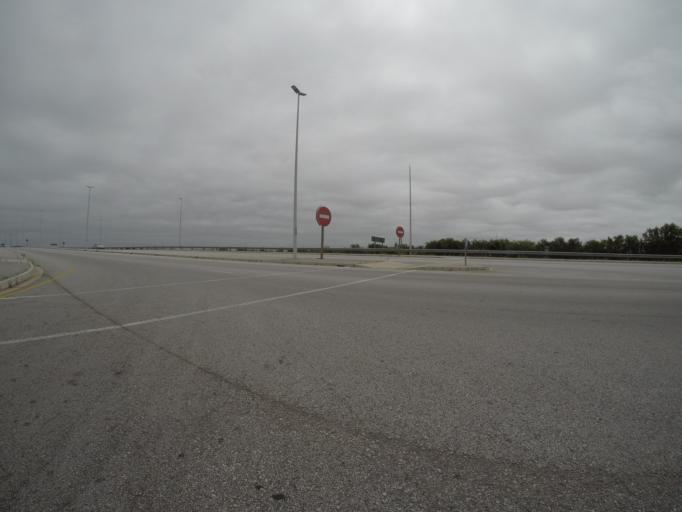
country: ZA
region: Eastern Cape
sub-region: Nelson Mandela Bay Metropolitan Municipality
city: Port Elizabeth
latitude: -33.9453
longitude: 25.4663
